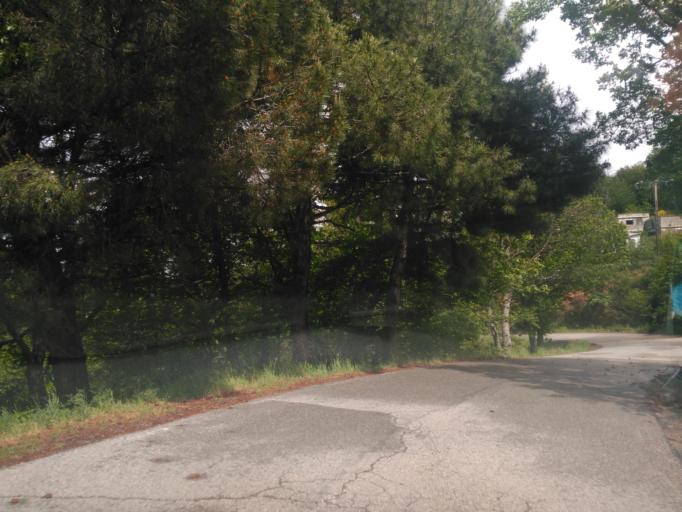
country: ES
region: Castille and Leon
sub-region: Provincia de Salamanca
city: Bejar
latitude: 40.3775
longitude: -5.7638
